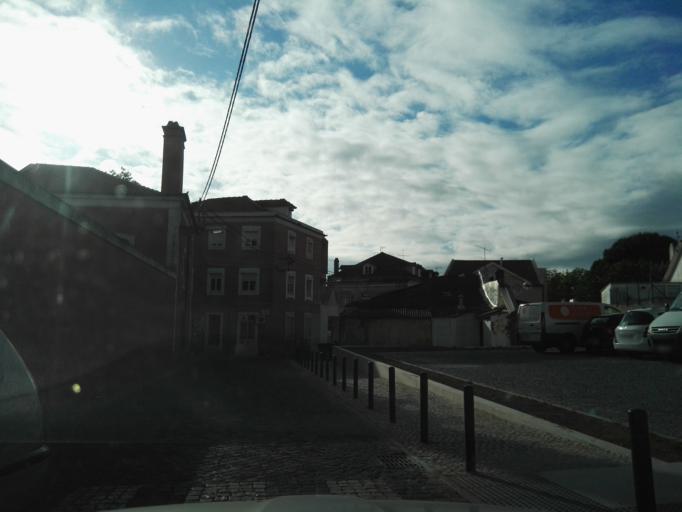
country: PT
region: Lisbon
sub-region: Odivelas
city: Olival do Basto
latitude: 38.7825
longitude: -9.1587
